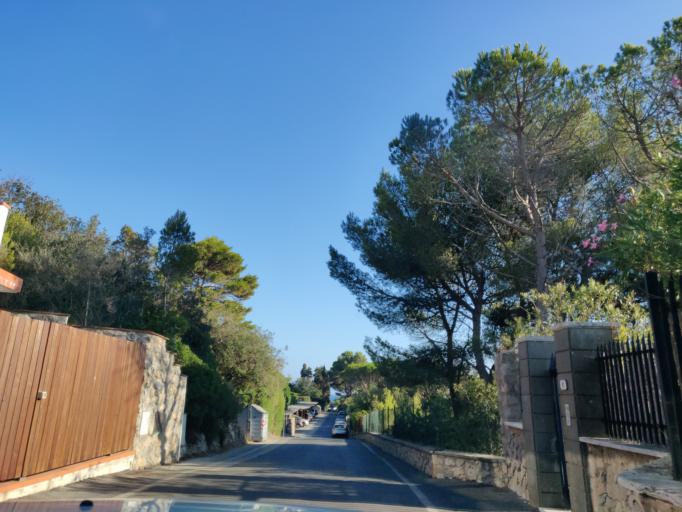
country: IT
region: Tuscany
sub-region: Provincia di Grosseto
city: Orbetello Scalo
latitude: 42.4121
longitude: 11.2805
